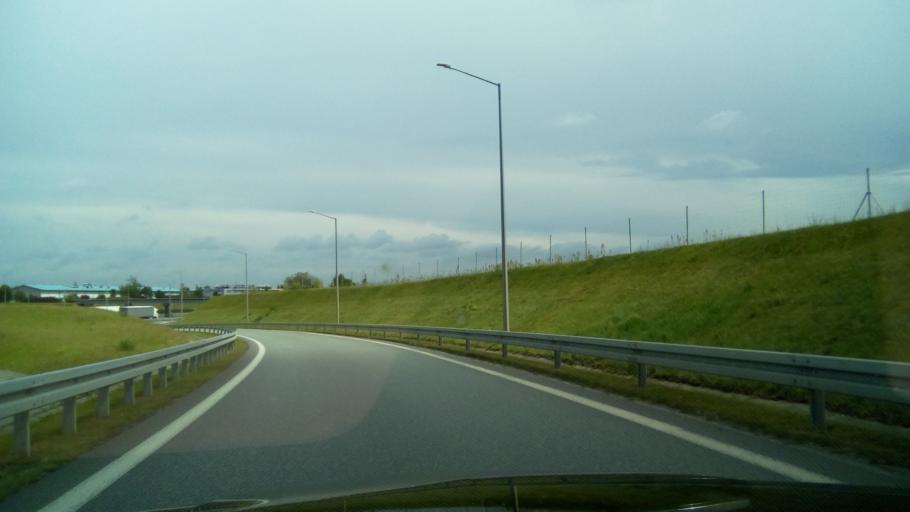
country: PL
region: Greater Poland Voivodeship
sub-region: Powiat poznanski
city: Komorniki
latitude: 52.3491
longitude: 16.8386
